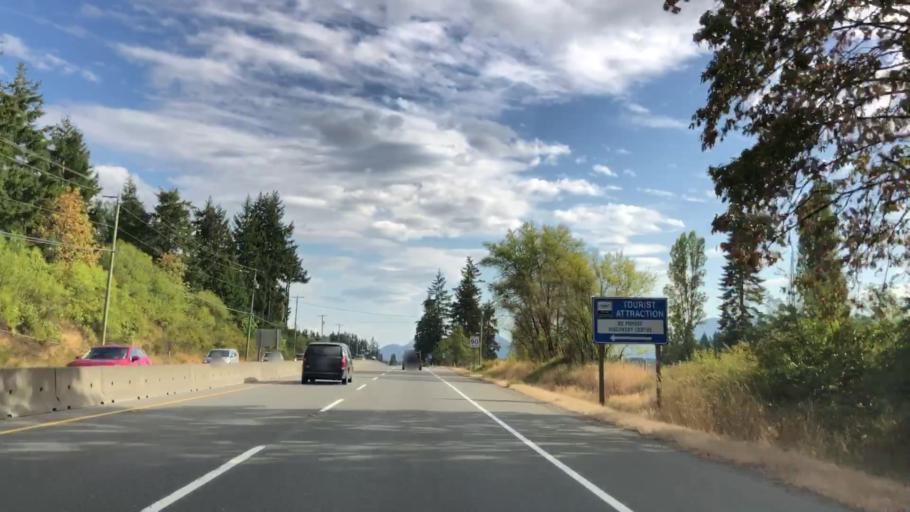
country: CA
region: British Columbia
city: Duncan
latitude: 48.8106
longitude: -123.7177
